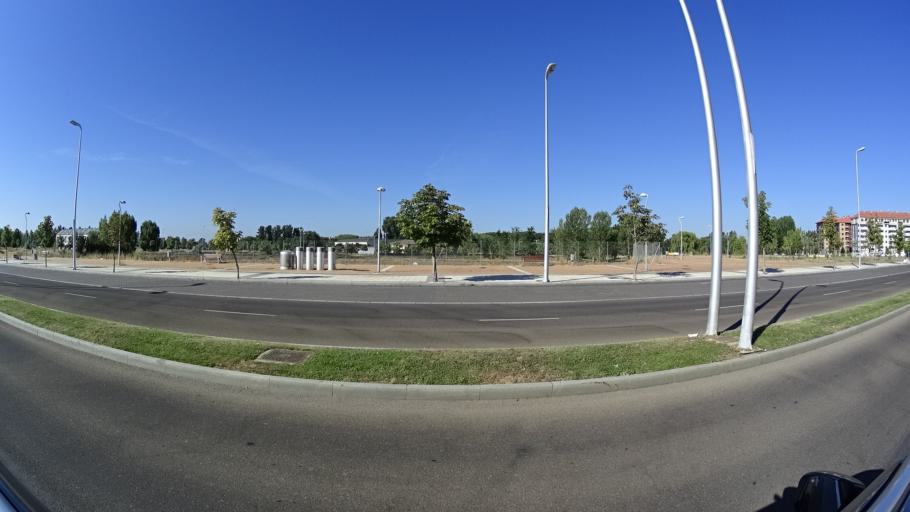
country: ES
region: Castille and Leon
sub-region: Provincia de Leon
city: Leon
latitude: 42.5810
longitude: -5.5637
